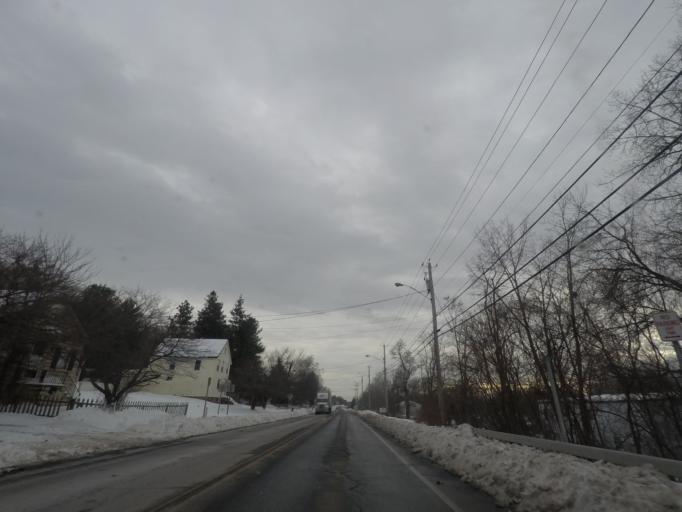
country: US
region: New York
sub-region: Rensselaer County
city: Rensselaer
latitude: 42.6268
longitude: -73.7443
